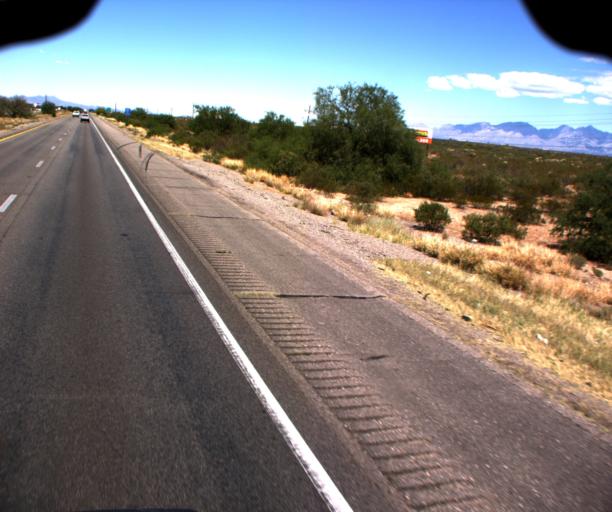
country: US
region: Arizona
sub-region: Pima County
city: Vail
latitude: 32.0693
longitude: -110.7858
